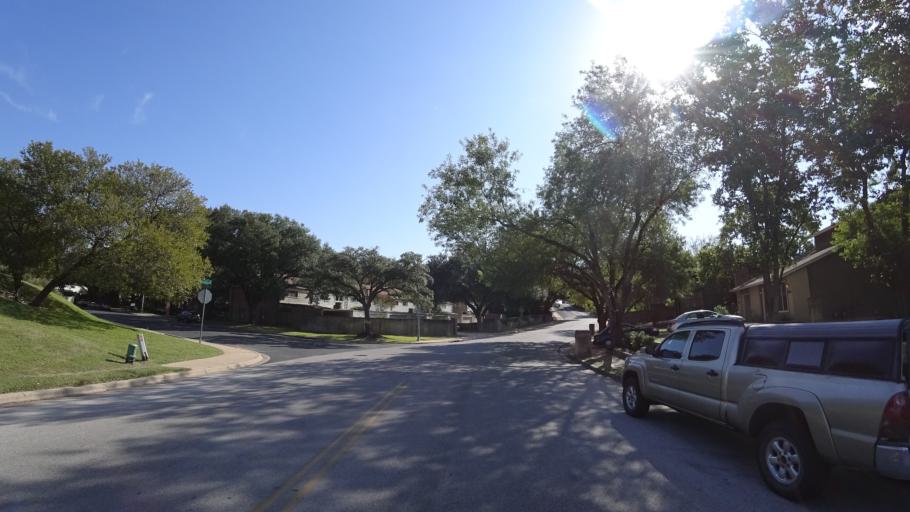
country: US
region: Texas
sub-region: Travis County
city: West Lake Hills
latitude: 30.3464
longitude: -97.7551
